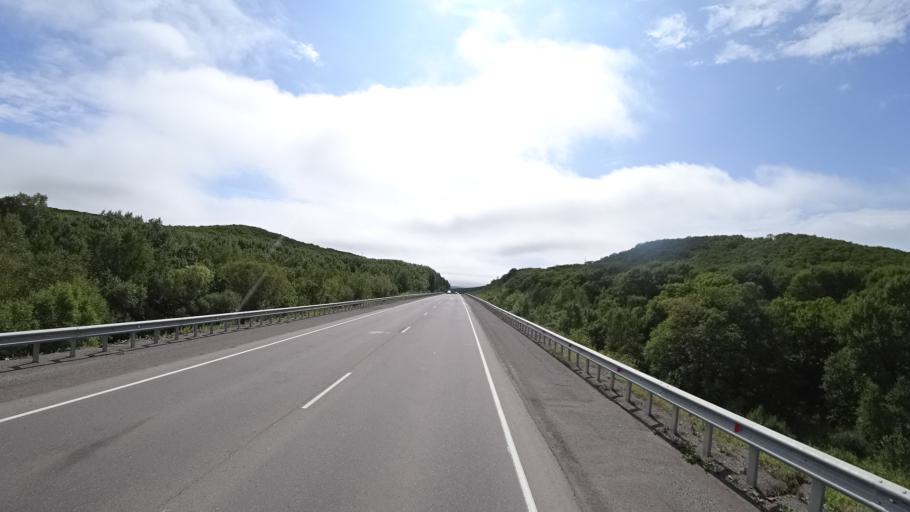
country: RU
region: Primorskiy
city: Lyalichi
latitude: 44.1264
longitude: 132.4243
